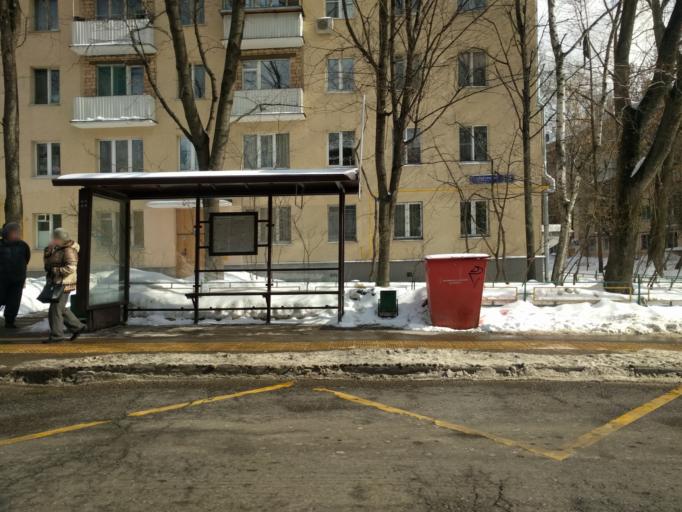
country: RU
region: Moscow
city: Metrogorodok
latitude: 55.7959
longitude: 37.7753
